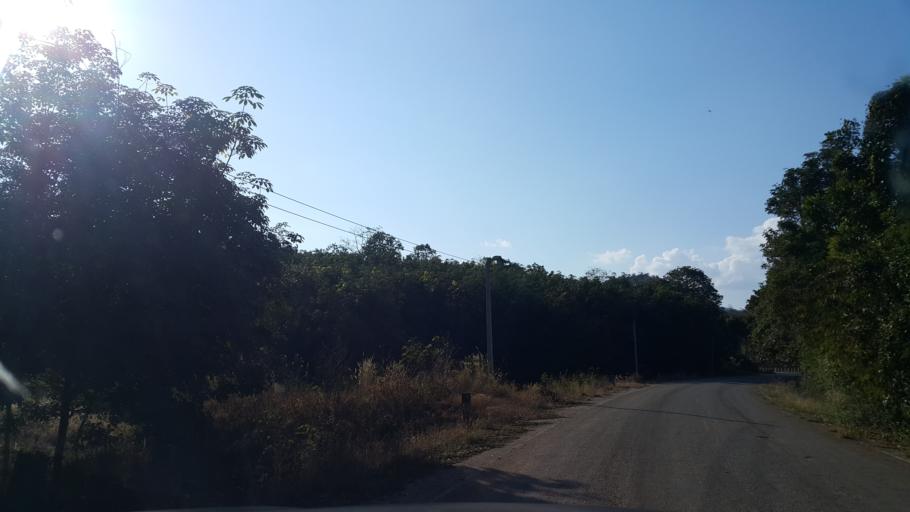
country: TH
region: Sukhothai
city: Thung Saliam
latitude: 17.3881
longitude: 99.5132
